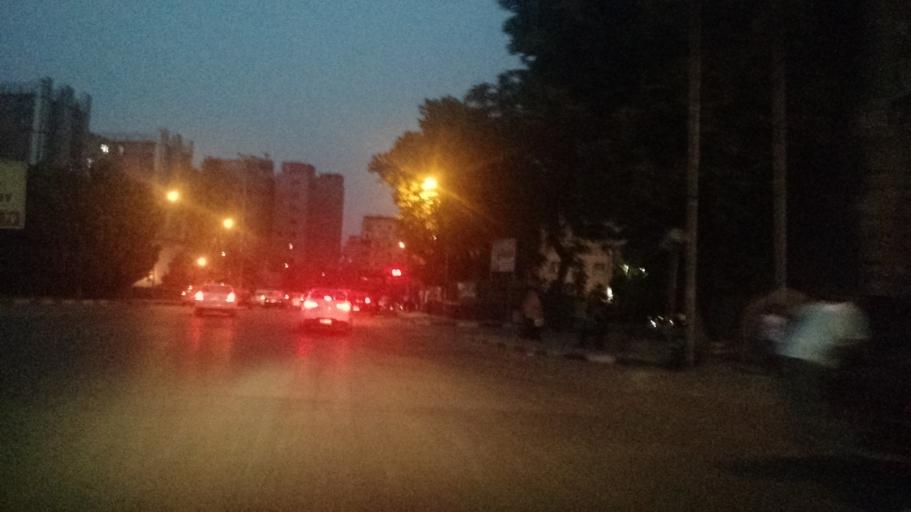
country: EG
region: Al Jizah
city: Al Jizah
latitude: 30.0289
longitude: 31.2295
